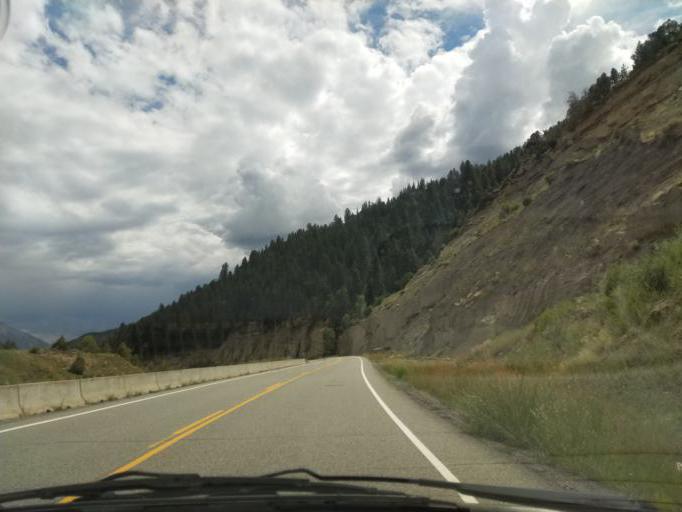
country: US
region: Colorado
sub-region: Delta County
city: Paonia
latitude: 39.0099
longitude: -107.3618
